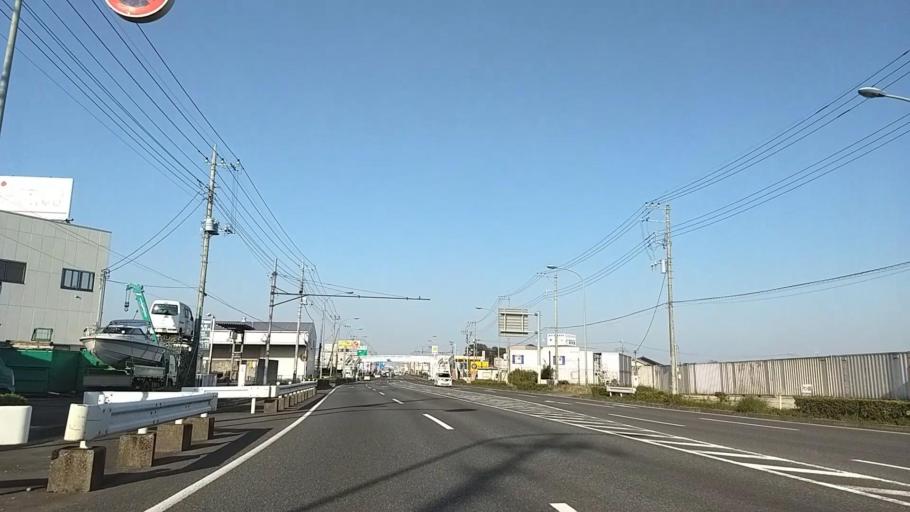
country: JP
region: Tokyo
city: Fussa
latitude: 35.7868
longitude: 139.3592
